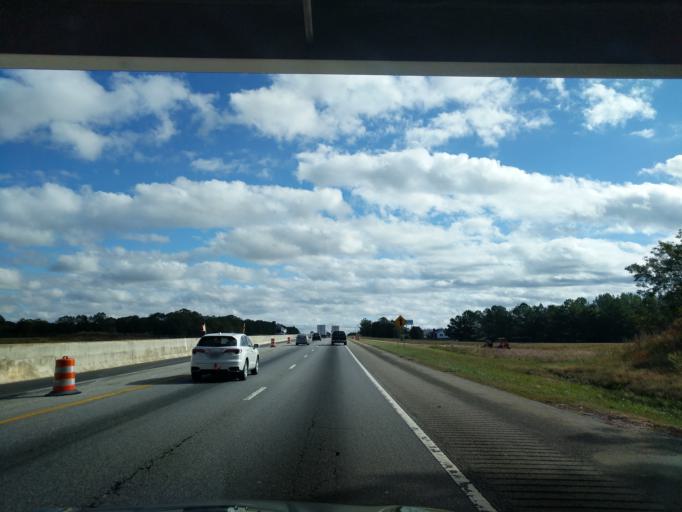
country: US
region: South Carolina
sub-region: Spartanburg County
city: Mayo
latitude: 35.0262
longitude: -81.8775
